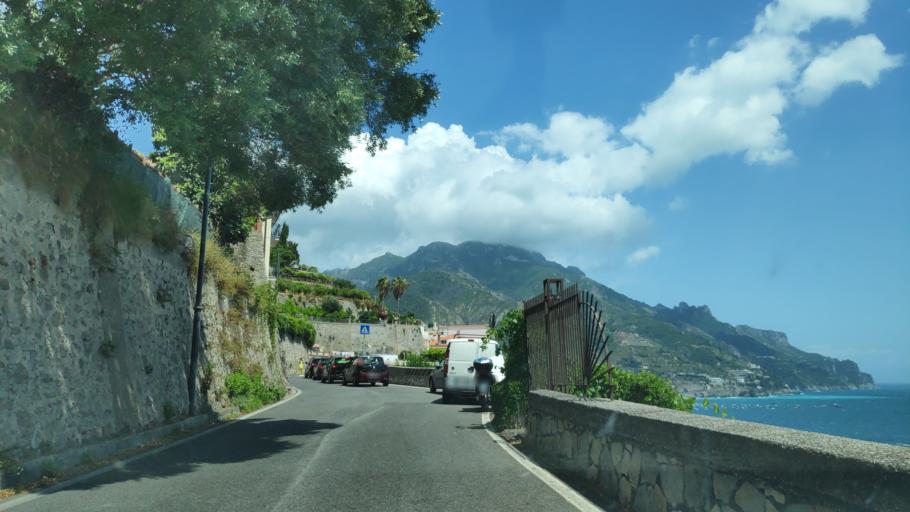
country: IT
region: Campania
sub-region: Provincia di Salerno
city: Minori
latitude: 40.6476
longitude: 14.6223
